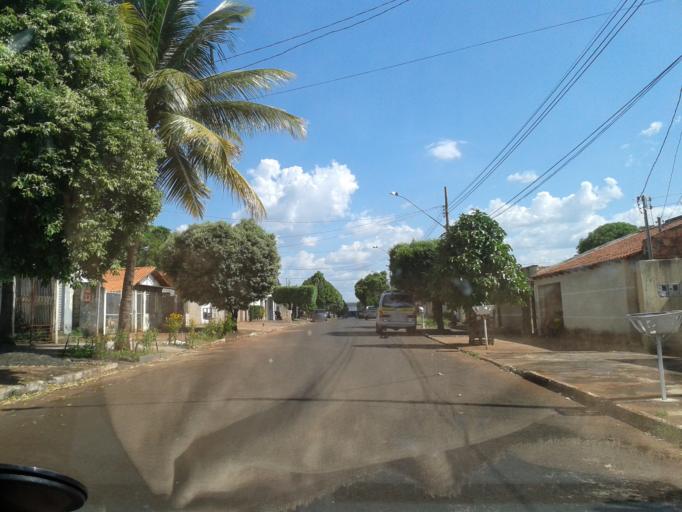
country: BR
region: Minas Gerais
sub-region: Ituiutaba
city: Ituiutaba
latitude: -18.9908
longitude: -49.4684
